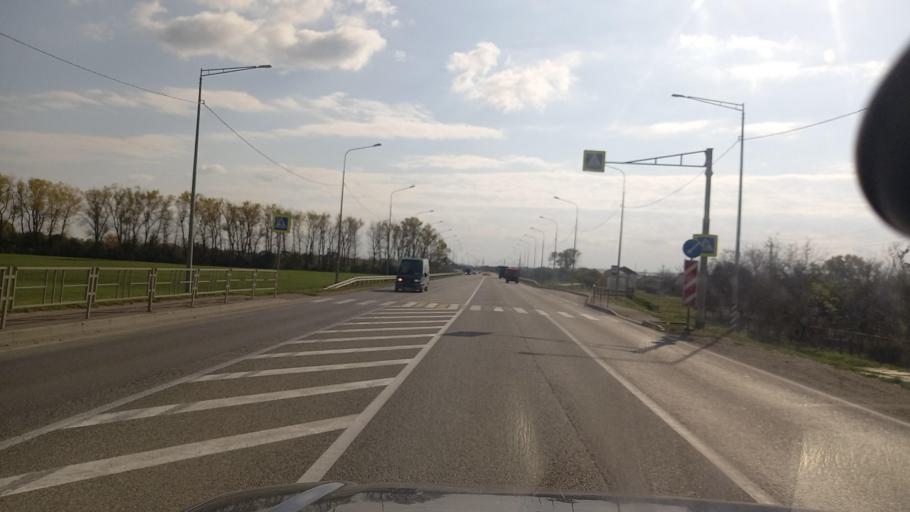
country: RU
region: Krasnodarskiy
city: Novoukrainskiy
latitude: 44.9026
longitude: 38.0342
